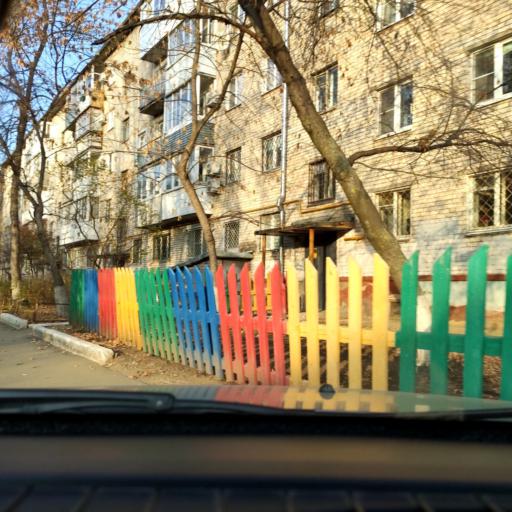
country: RU
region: Samara
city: Tol'yatti
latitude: 53.5022
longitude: 49.4032
